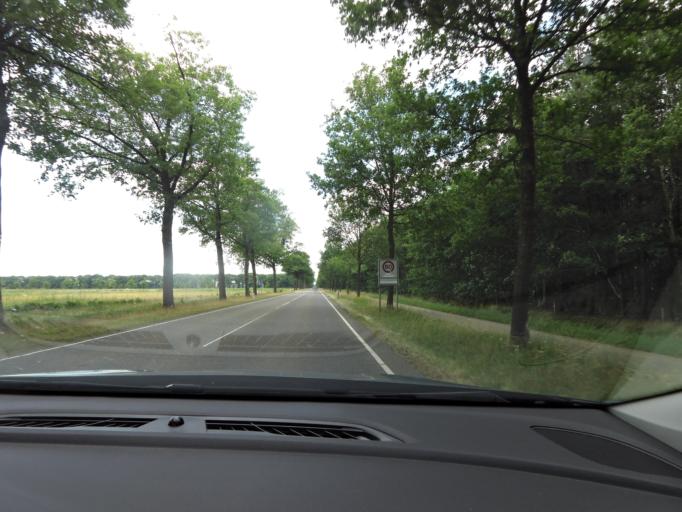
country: NL
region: North Brabant
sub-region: Gemeente Baarle-Nassau
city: Baarle-Nassau
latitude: 51.4705
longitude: 4.9002
